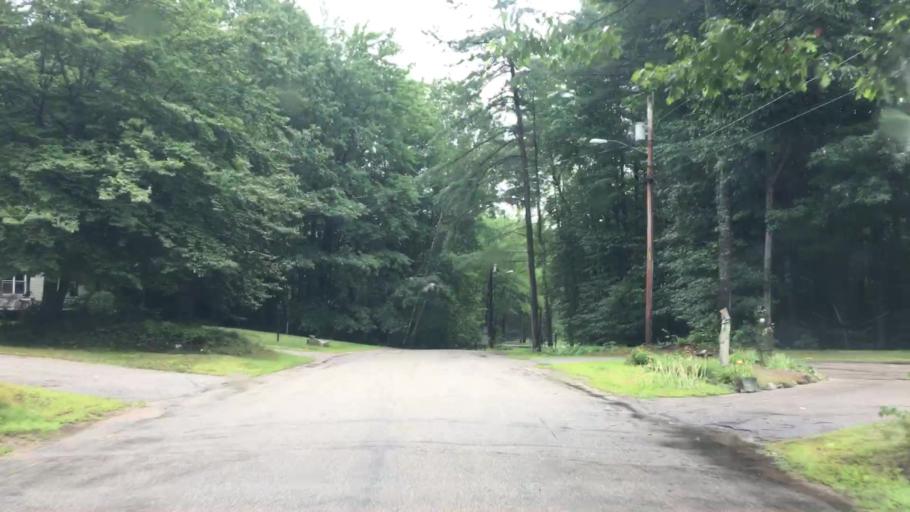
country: US
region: New Hampshire
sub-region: Carroll County
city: Conway
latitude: 43.9904
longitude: -71.0994
